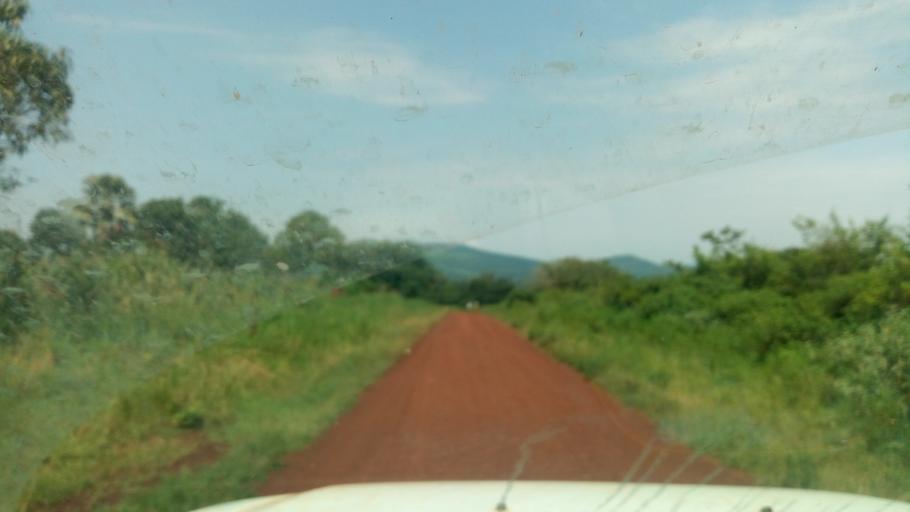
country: UG
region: Western Region
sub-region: Masindi District
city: Masindi
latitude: 1.6648
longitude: 31.8162
